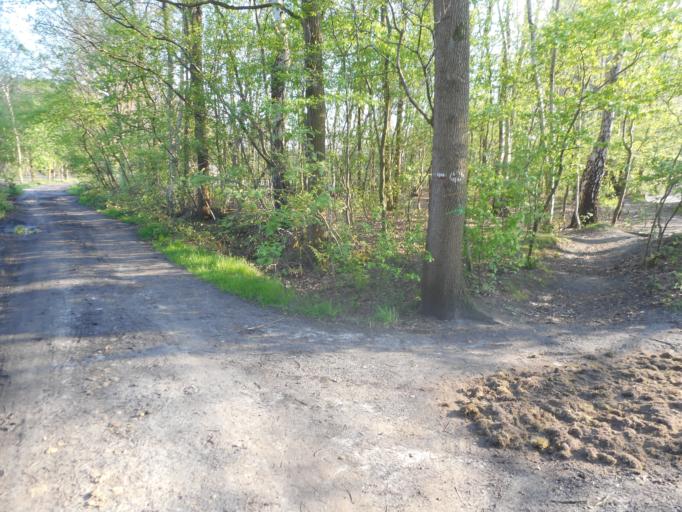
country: BE
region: Flanders
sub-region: Provincie Antwerpen
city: Schilde
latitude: 51.2244
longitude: 4.6180
